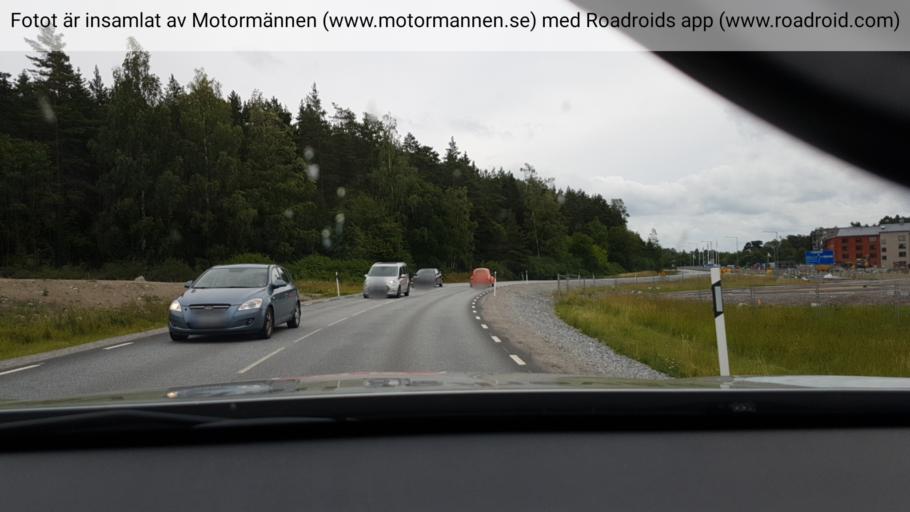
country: SE
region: Stockholm
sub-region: Sigtuna Kommun
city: Sigtuna
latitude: 59.6309
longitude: 17.7192
